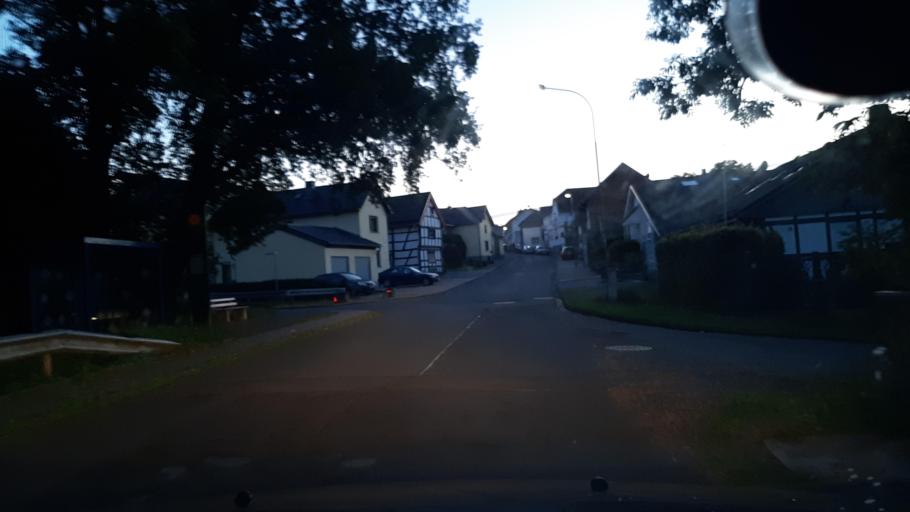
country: DE
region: North Rhine-Westphalia
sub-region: Regierungsbezirk Koln
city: Bad Munstereifel
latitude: 50.5484
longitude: 6.7262
